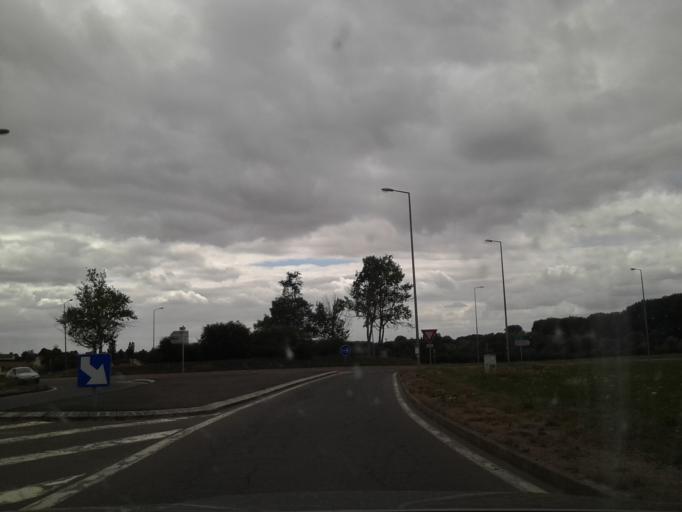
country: FR
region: Centre
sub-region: Departement du Cher
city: Saint-Doulchard
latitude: 47.0819
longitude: 2.3552
